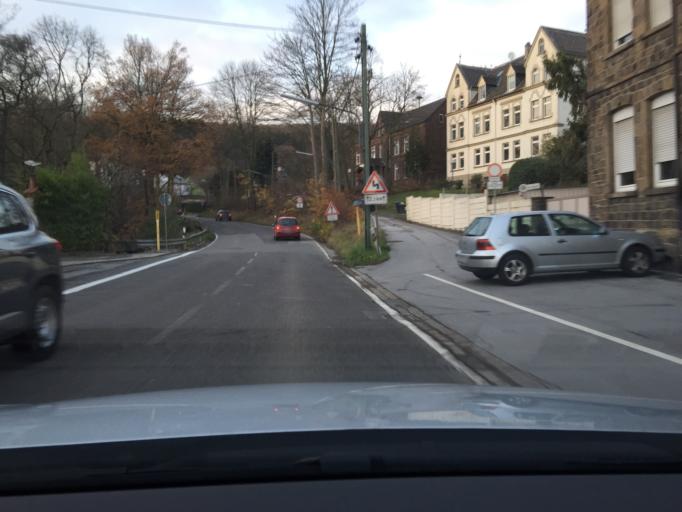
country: DE
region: North Rhine-Westphalia
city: Hattingen
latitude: 51.3745
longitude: 7.1353
